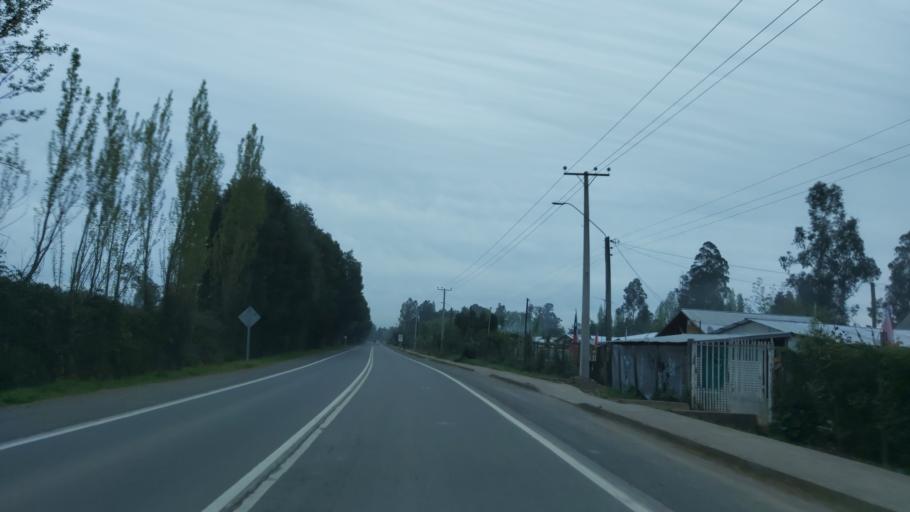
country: CL
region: Maule
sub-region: Provincia de Linares
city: Colbun
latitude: -35.7566
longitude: -71.5017
